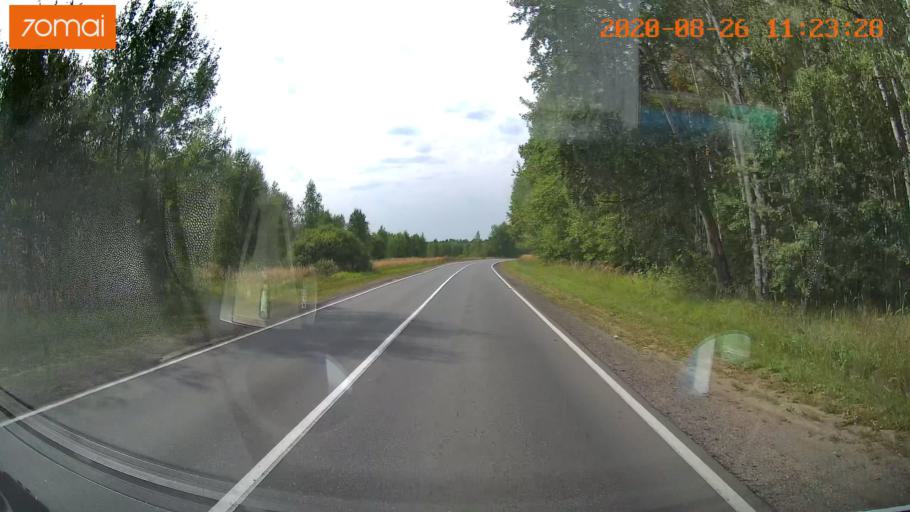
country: RU
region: Rjazan
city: Shilovo
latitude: 54.3518
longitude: 41.0100
